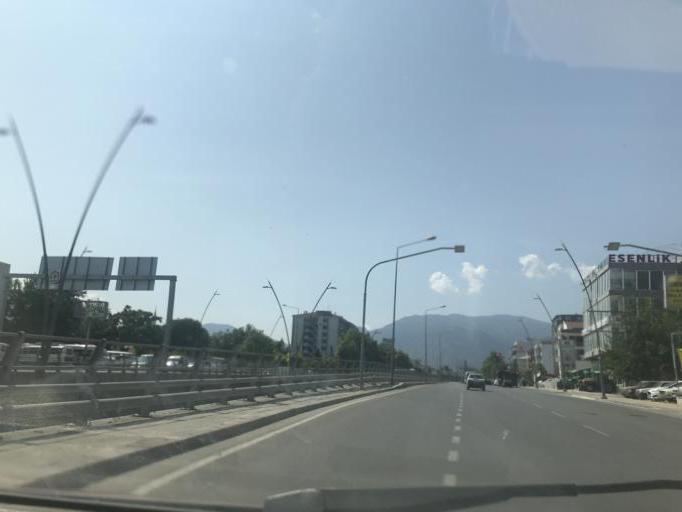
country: TR
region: Denizli
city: Denizli
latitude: 37.7799
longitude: 29.0973
